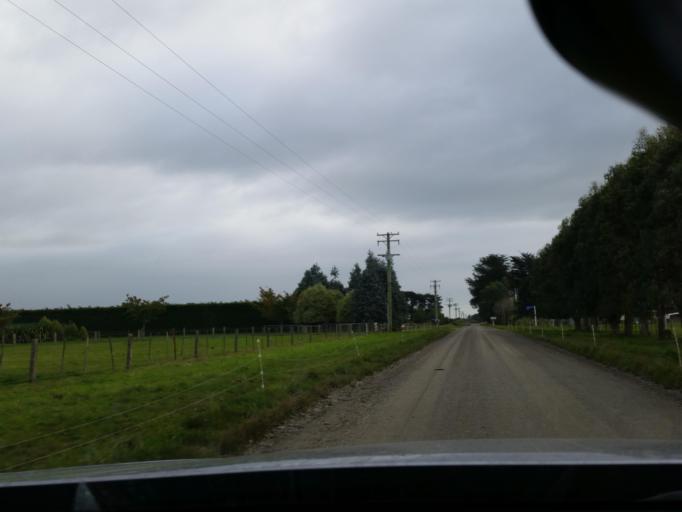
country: NZ
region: Southland
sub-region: Invercargill City
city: Invercargill
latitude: -46.3557
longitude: 168.4466
